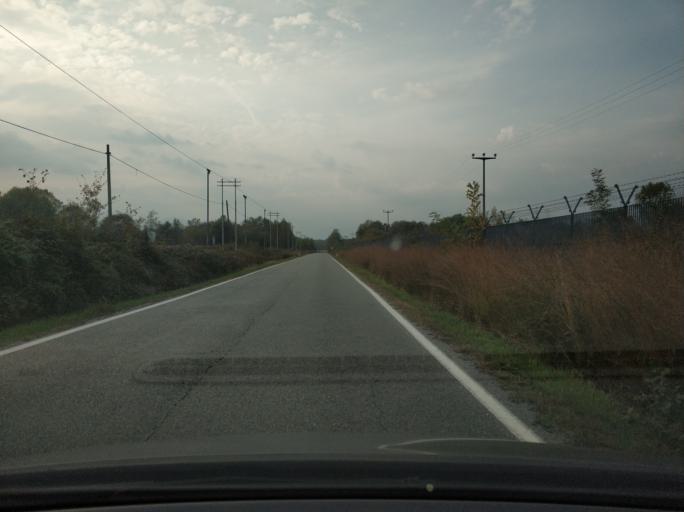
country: IT
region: Piedmont
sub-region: Provincia di Torino
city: San Francesco al Campo
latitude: 45.2454
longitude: 7.6600
